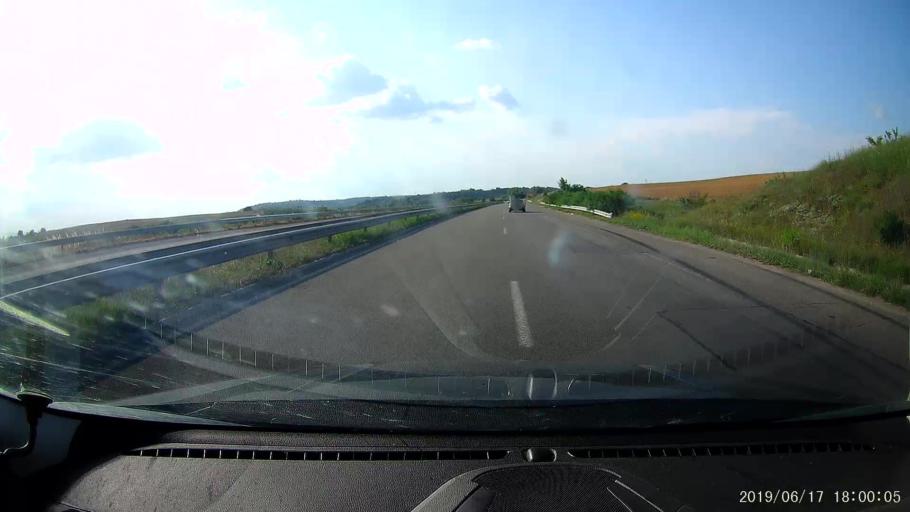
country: BG
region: Khaskovo
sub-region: Obshtina Svilengrad
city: Svilengrad
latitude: 41.7311
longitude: 26.2842
